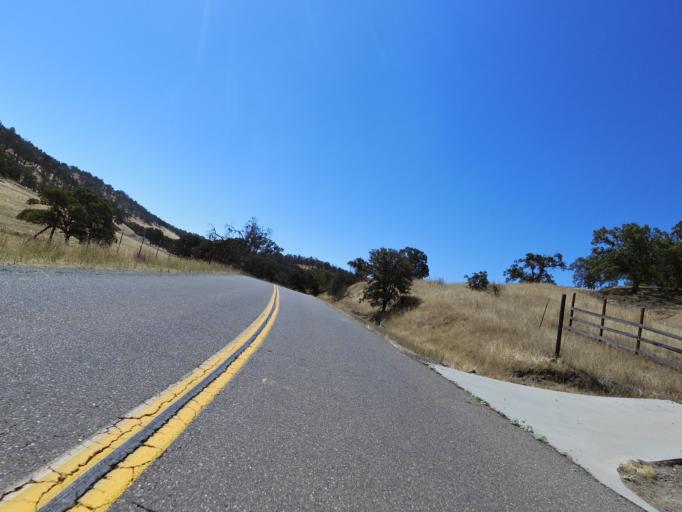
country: US
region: California
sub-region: Tuolumne County
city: Tuolumne City
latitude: 37.6693
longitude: -120.3169
